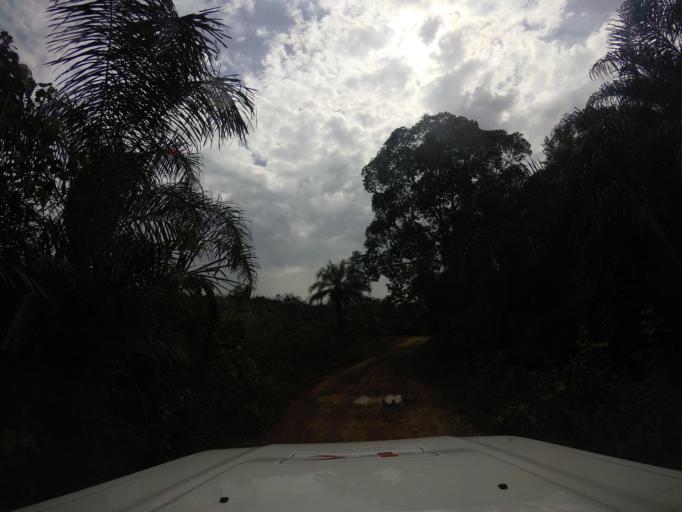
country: SL
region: Southern Province
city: Zimmi
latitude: 7.2125
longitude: -11.1946
